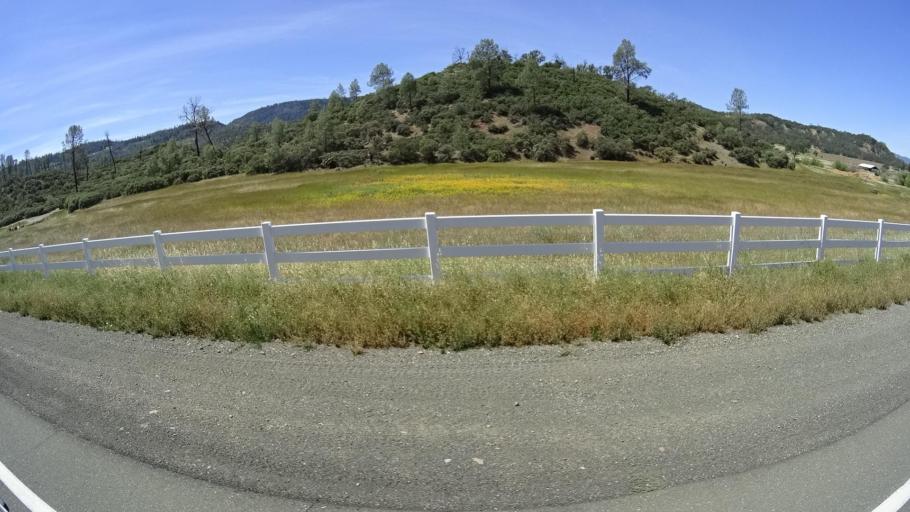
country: US
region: California
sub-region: Lake County
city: Hidden Valley Lake
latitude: 38.7248
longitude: -122.5125
